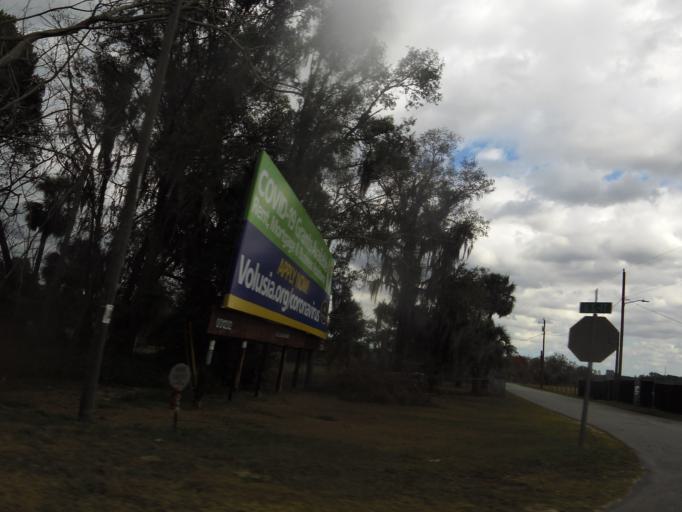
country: US
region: Florida
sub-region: Volusia County
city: Pierson
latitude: 29.3142
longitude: -81.4915
